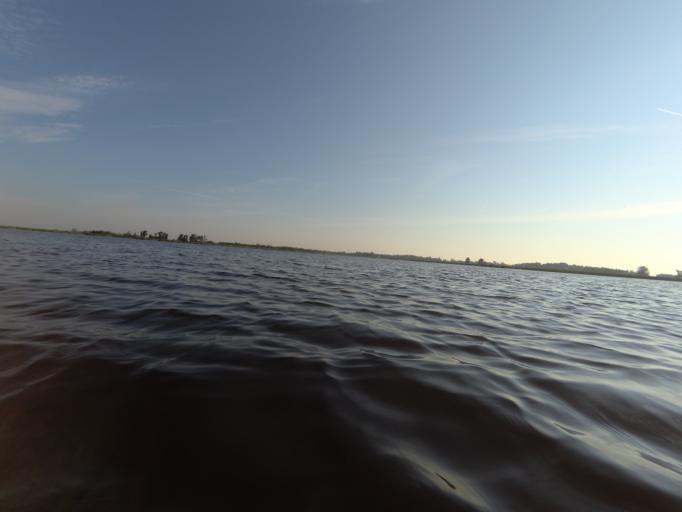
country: NL
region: Overijssel
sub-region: Gemeente Steenwijkerland
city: Sint Jansklooster
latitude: 52.6800
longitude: 6.0312
